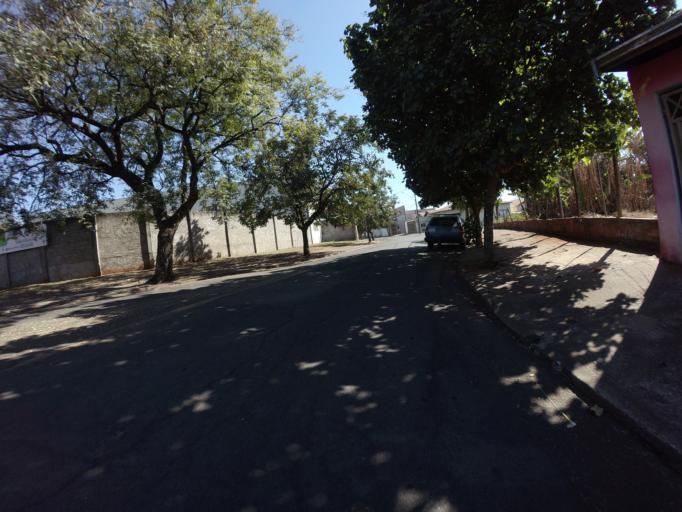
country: BR
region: Sao Paulo
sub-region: Piracicaba
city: Piracicaba
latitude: -22.7679
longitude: -47.5866
